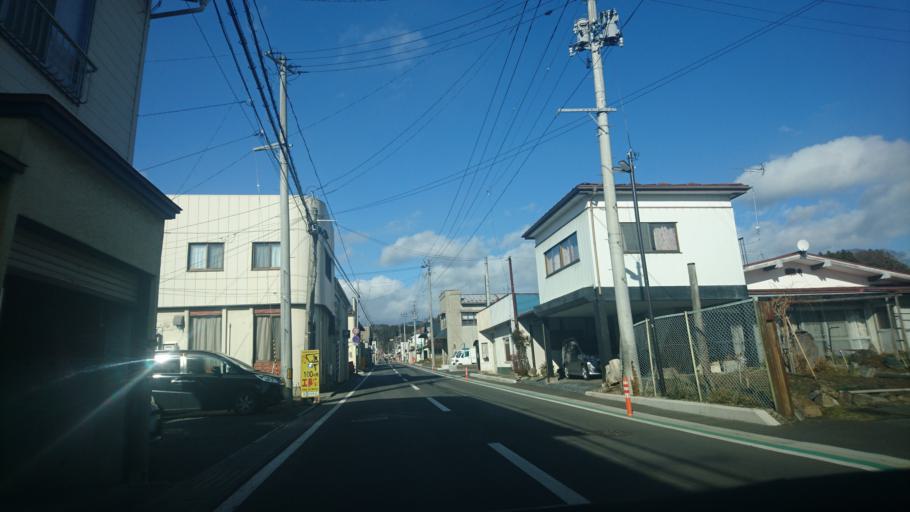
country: JP
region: Iwate
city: Mizusawa
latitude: 39.0496
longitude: 141.3670
